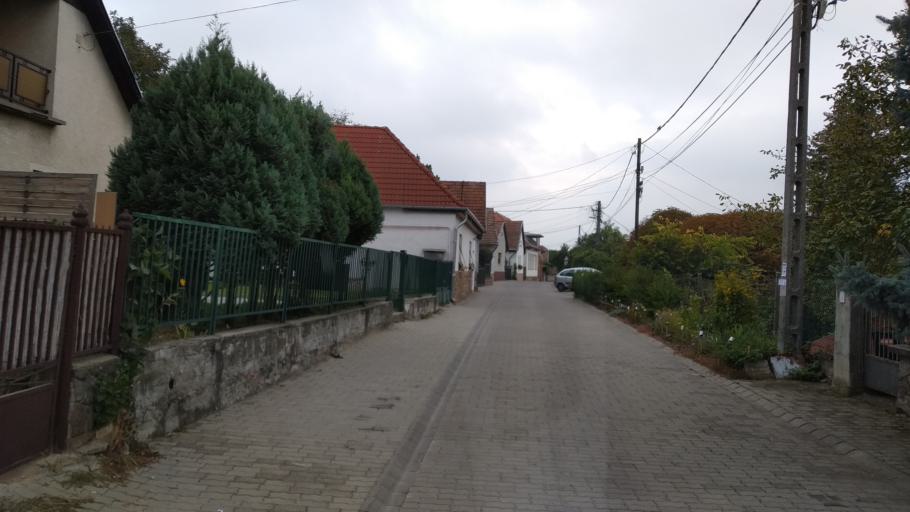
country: HU
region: Pest
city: Solymar
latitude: 47.5945
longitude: 18.9340
